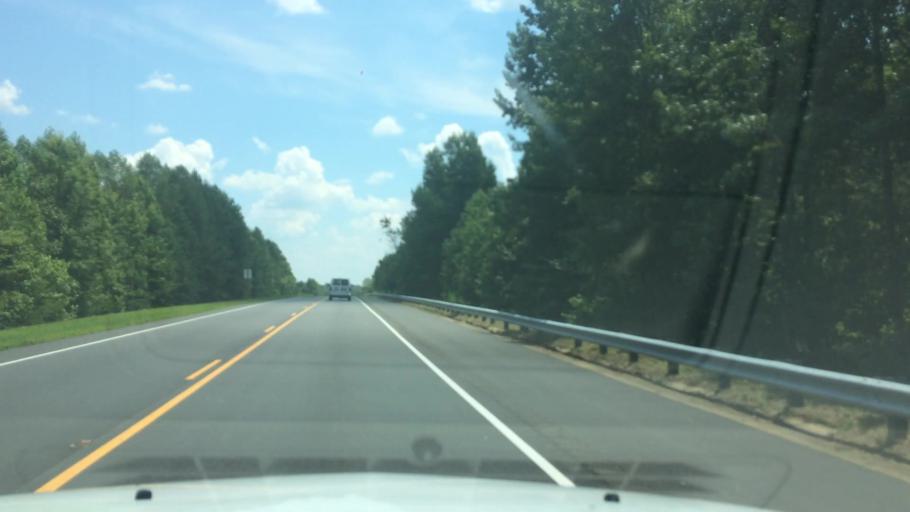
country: US
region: North Carolina
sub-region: Alexander County
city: Stony Point
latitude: 35.8391
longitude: -81.0233
